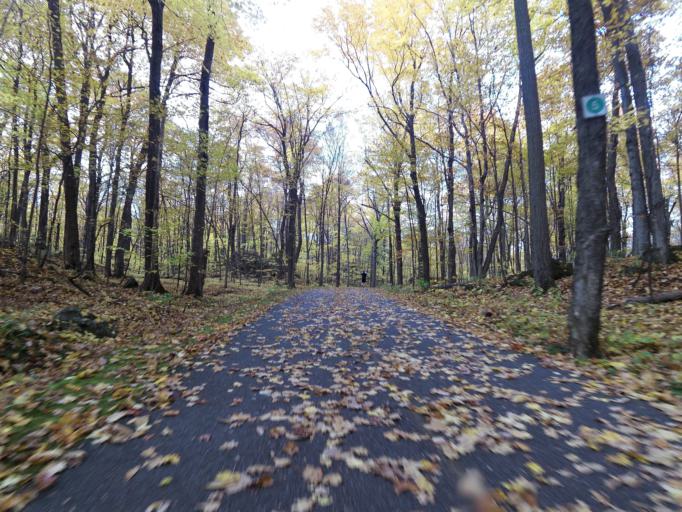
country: CA
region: Quebec
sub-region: Outaouais
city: Gatineau
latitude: 45.4596
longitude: -75.7819
